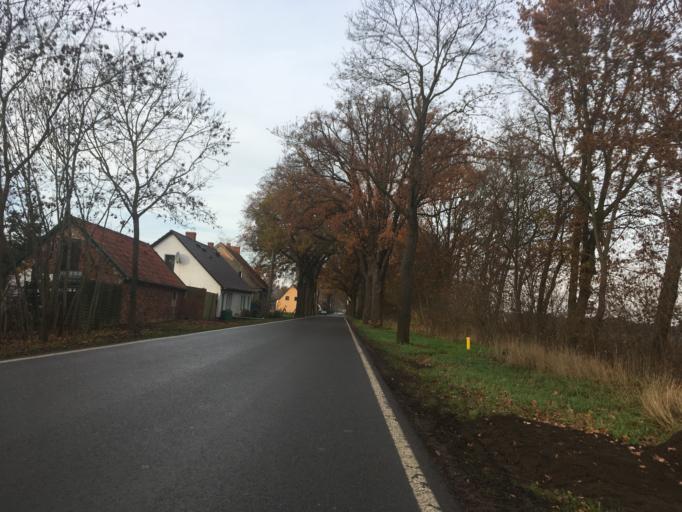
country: DE
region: Brandenburg
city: Neulewin
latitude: 52.7216
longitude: 14.2859
